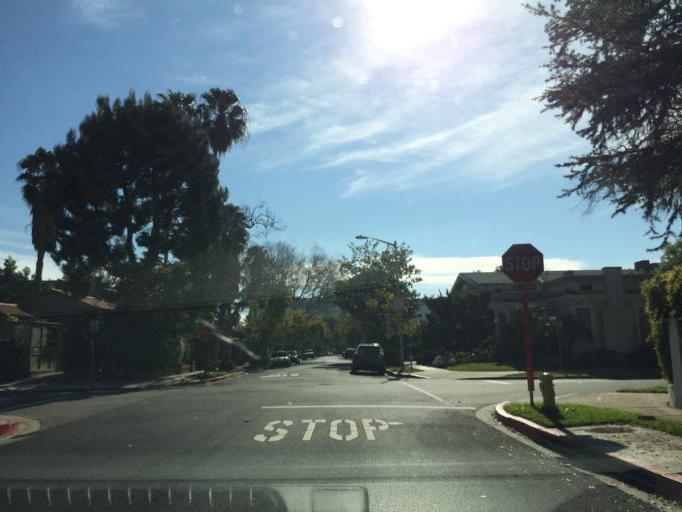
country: US
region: California
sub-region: Los Angeles County
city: West Hollywood
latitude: 34.0796
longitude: -118.3797
